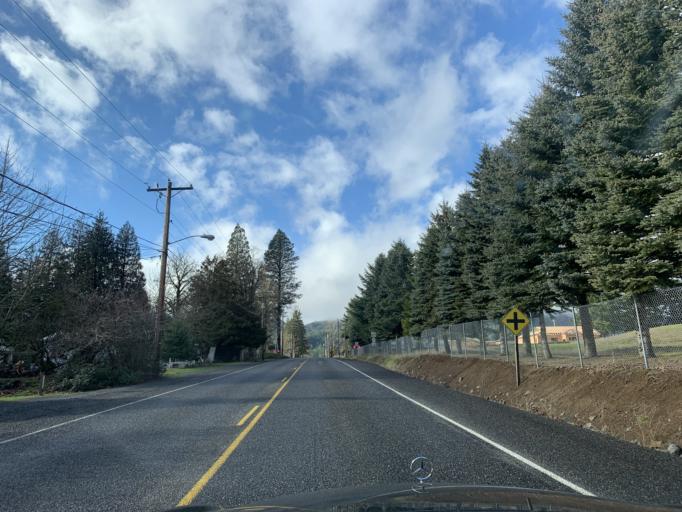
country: US
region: Washington
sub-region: Skamania County
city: Carson
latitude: 45.7261
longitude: -121.8077
